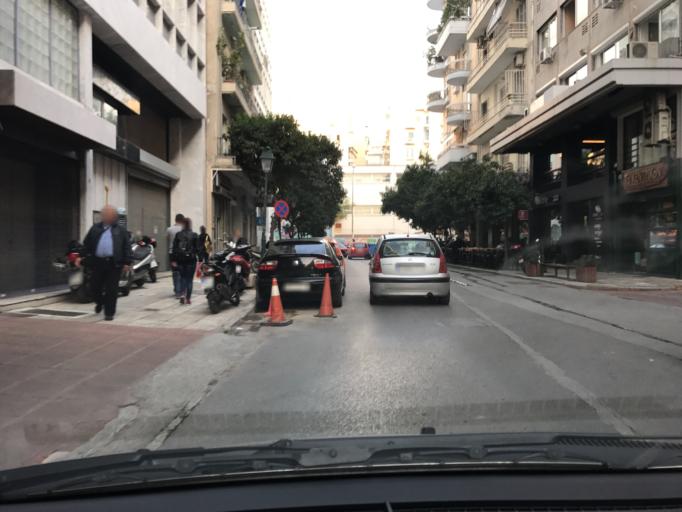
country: GR
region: Central Macedonia
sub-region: Nomos Thessalonikis
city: Thessaloniki
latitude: 40.6336
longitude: 22.9436
